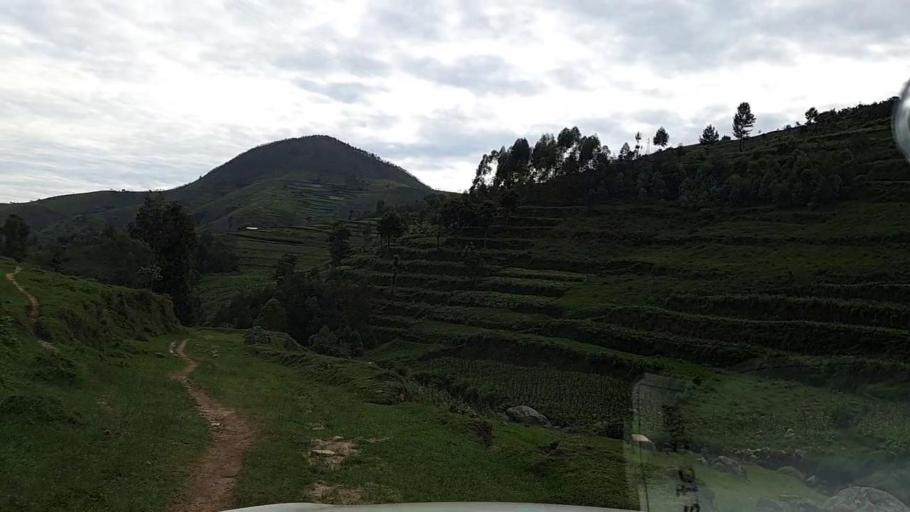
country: RW
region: Southern Province
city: Nzega
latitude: -2.4049
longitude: 29.4999
